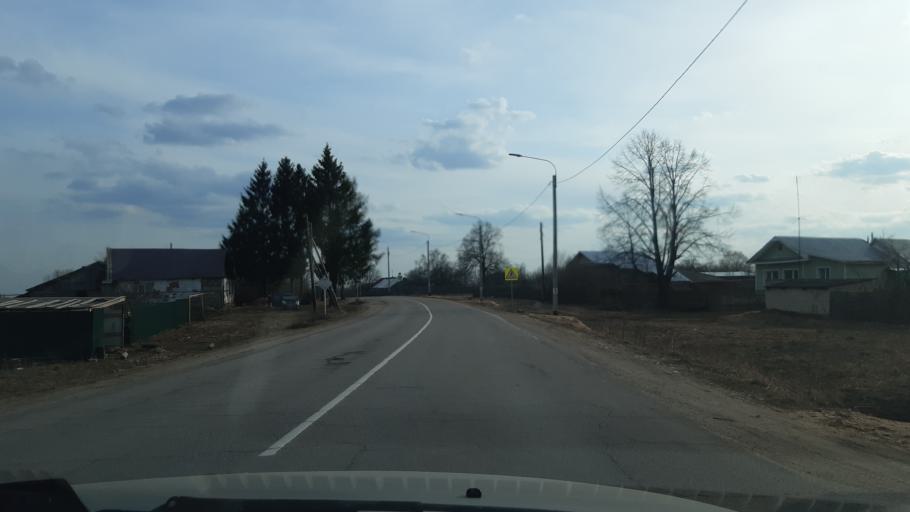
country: RU
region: Vladimir
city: Nikologory
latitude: 56.1622
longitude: 41.9959
